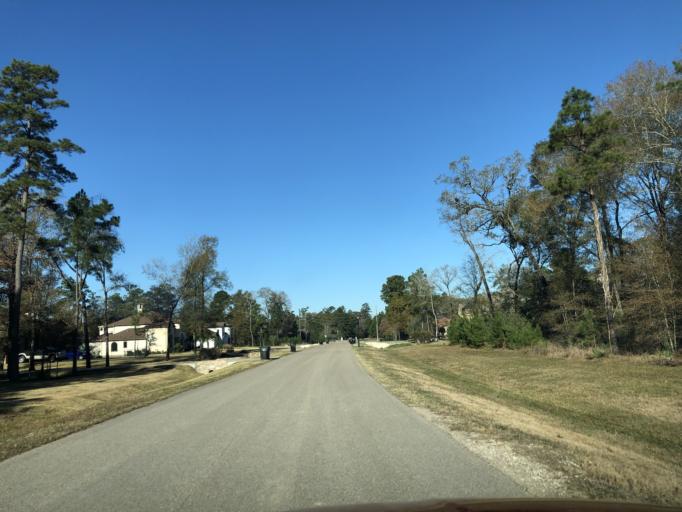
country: US
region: Texas
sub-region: Montgomery County
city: Porter Heights
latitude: 30.0753
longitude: -95.3337
